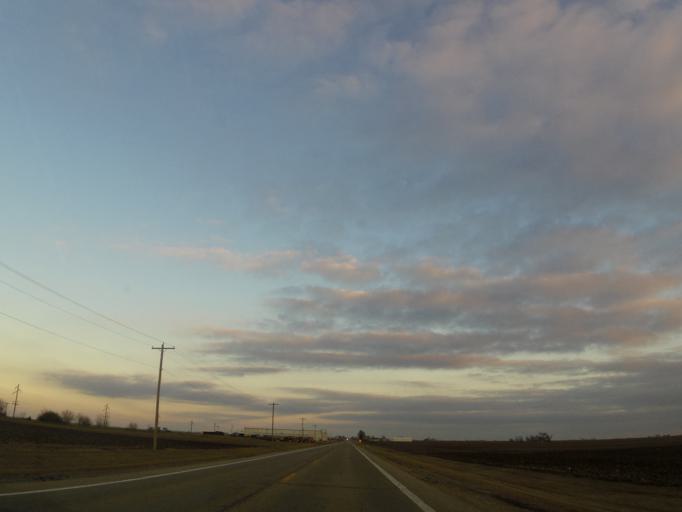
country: US
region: Illinois
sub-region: Woodford County
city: El Paso
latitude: 40.7380
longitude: -88.9833
